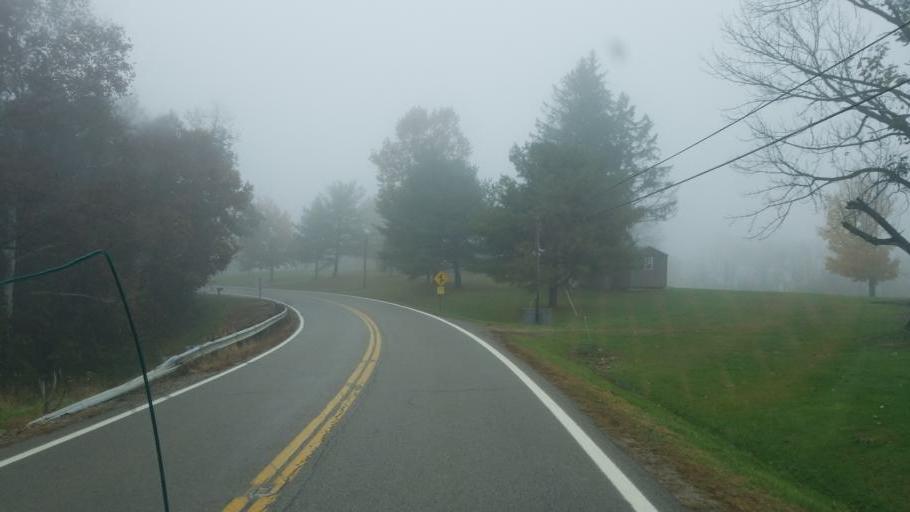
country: US
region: Ohio
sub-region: Morgan County
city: McConnelsville
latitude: 39.6217
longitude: -81.8800
